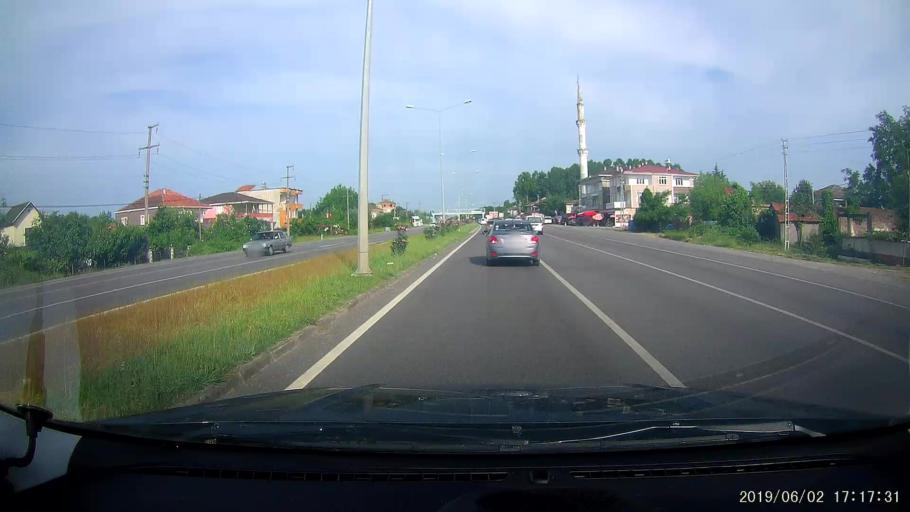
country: TR
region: Samsun
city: Dikbiyik
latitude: 41.2282
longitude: 36.5834
